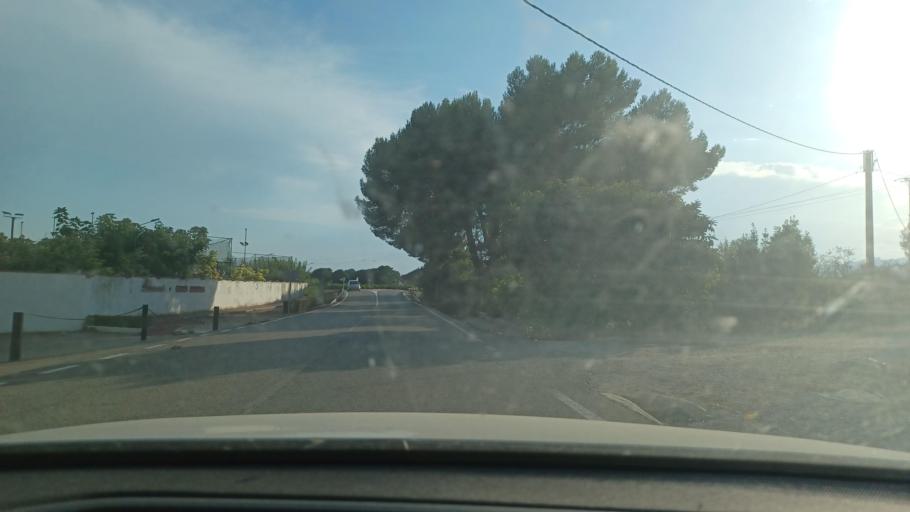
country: ES
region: Catalonia
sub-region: Provincia de Tarragona
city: Santa Barbara
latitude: 40.7120
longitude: 0.4872
